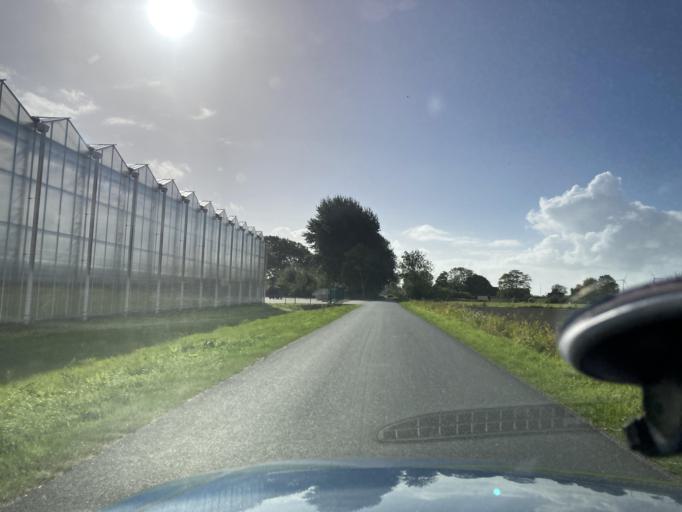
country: DE
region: Schleswig-Holstein
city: Wohrden
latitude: 54.1720
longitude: 9.0108
